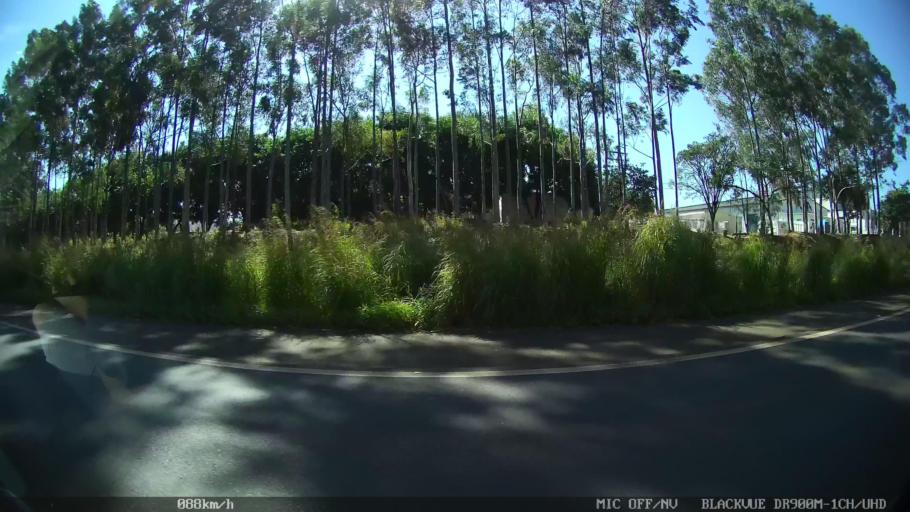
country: BR
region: Sao Paulo
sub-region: Franca
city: Franca
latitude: -20.5570
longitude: -47.4455
